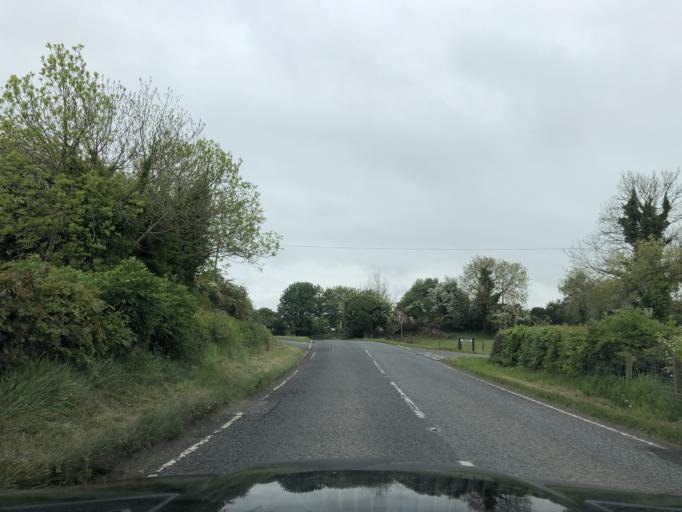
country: GB
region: Northern Ireland
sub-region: Down District
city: Portaferry
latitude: 54.3613
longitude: -5.6025
